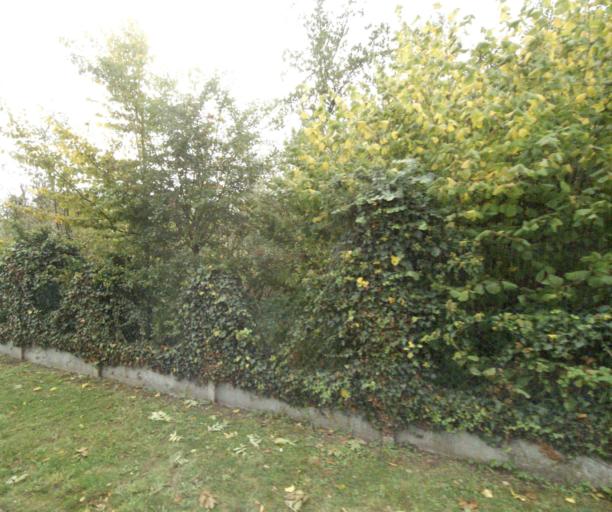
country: FR
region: Nord-Pas-de-Calais
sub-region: Departement du Nord
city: Erquinghem-Lys
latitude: 50.6814
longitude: 2.8546
